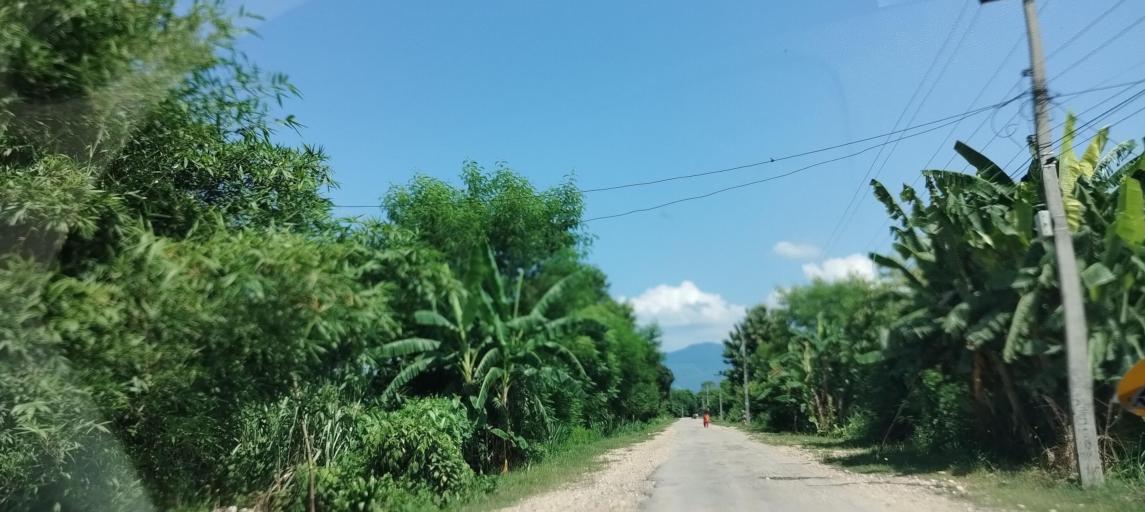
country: NP
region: Far Western
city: Tikapur
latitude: 28.5007
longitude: 81.3016
